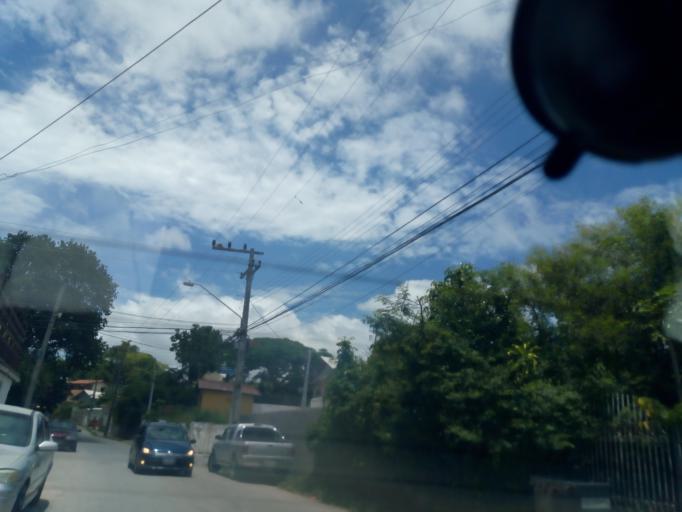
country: BR
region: Santa Catarina
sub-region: Florianopolis
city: Itacorubi
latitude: -27.3952
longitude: -48.4243
